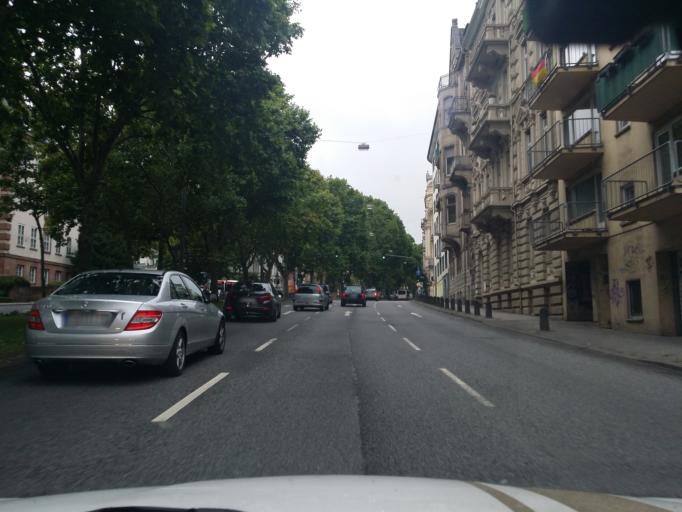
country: DE
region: Hesse
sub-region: Regierungsbezirk Darmstadt
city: Wiesbaden
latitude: 50.0717
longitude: 8.2387
